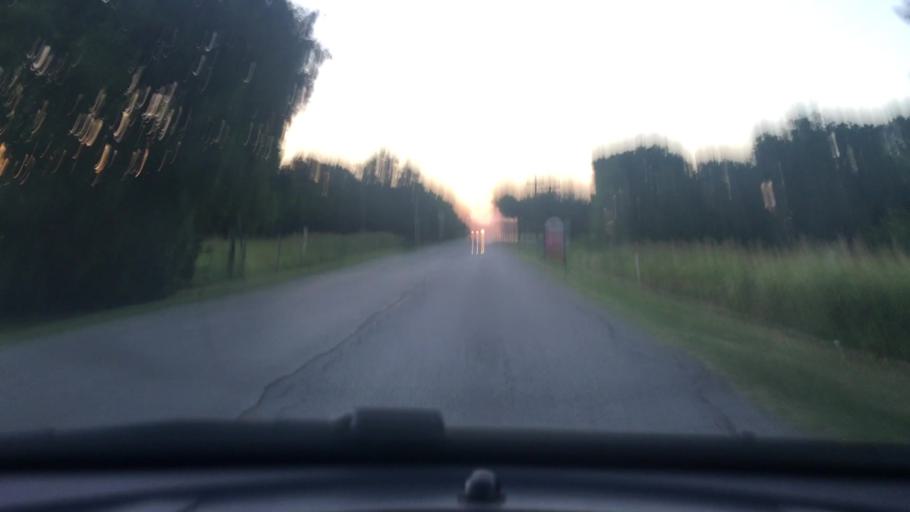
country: US
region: Texas
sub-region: Ellis County
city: Red Oak
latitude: 32.5607
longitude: -96.8069
